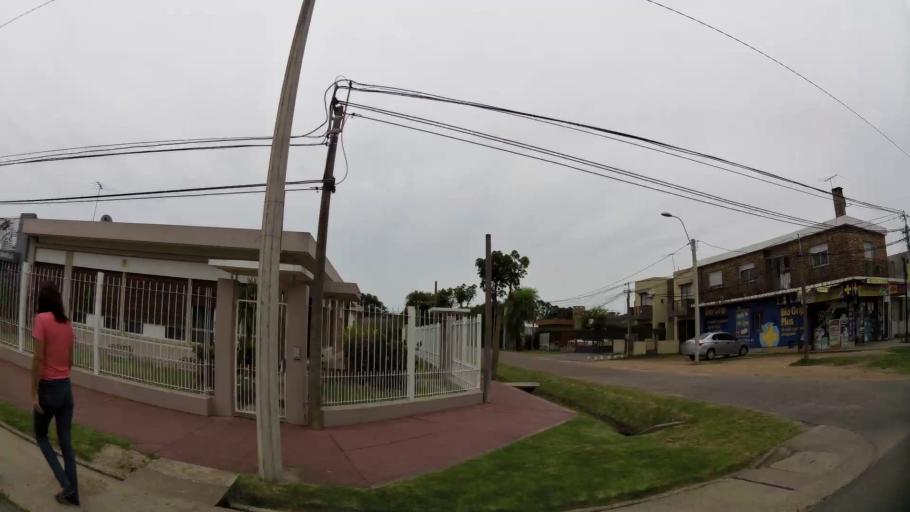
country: UY
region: Canelones
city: Las Piedras
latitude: -34.7274
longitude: -56.2269
